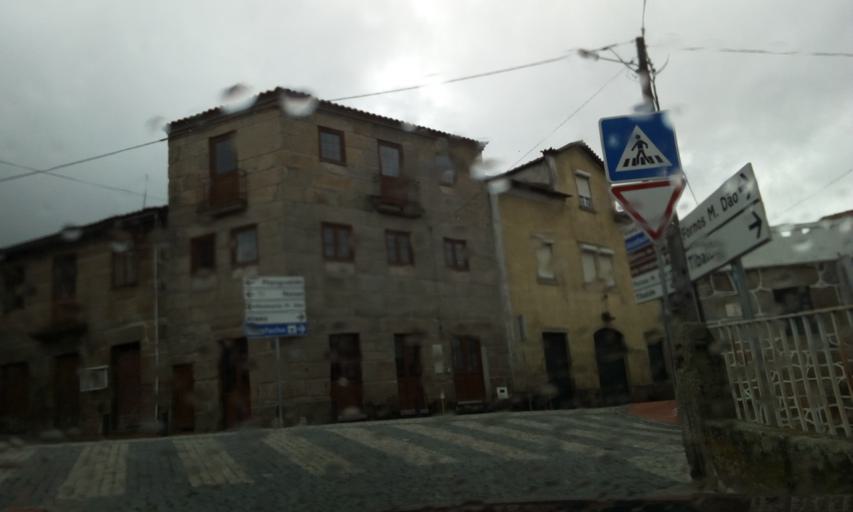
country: PT
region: Viseu
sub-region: Nelas
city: Nelas
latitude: 40.6005
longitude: -7.8442
